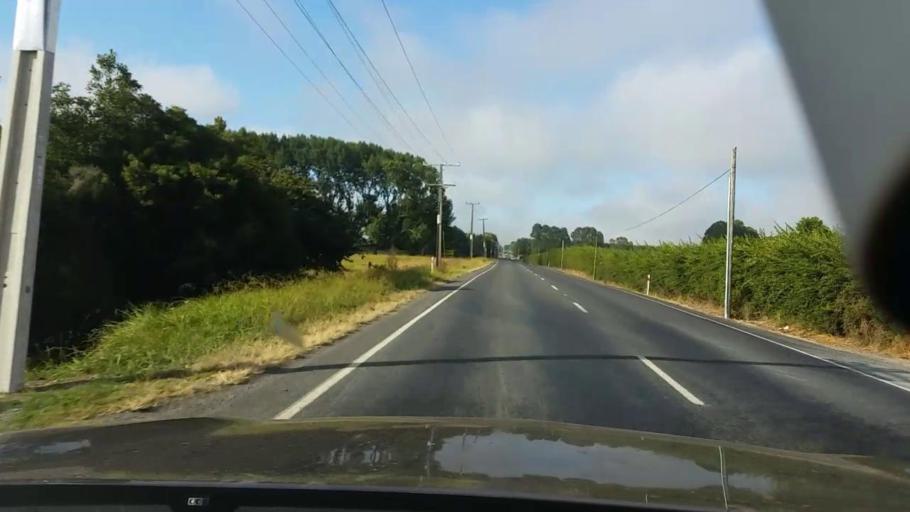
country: NZ
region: Waikato
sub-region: Hamilton City
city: Hamilton
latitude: -37.6006
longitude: 175.3526
